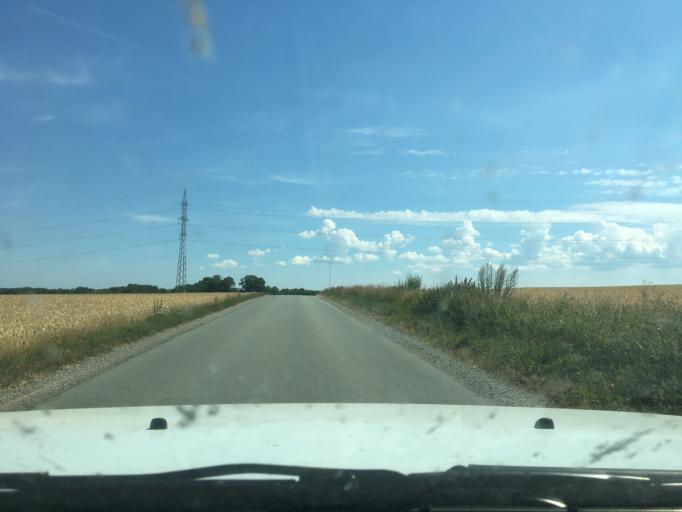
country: DK
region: Central Jutland
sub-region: Randers Kommune
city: Assentoft
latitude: 56.3620
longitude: 10.1304
